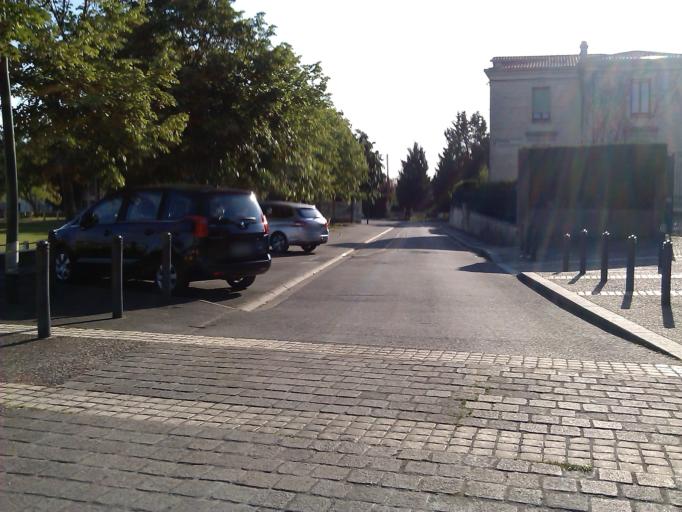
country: FR
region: Aquitaine
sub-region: Departement de la Gironde
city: Cubzac-les-Ponts
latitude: 44.9913
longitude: -0.4499
